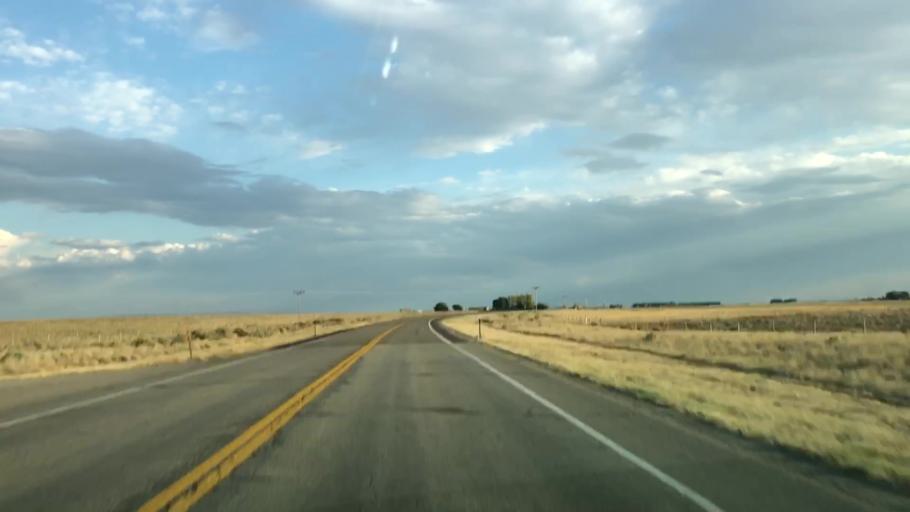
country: US
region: Wyoming
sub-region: Sweetwater County
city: North Rock Springs
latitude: 42.0875
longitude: -109.4396
